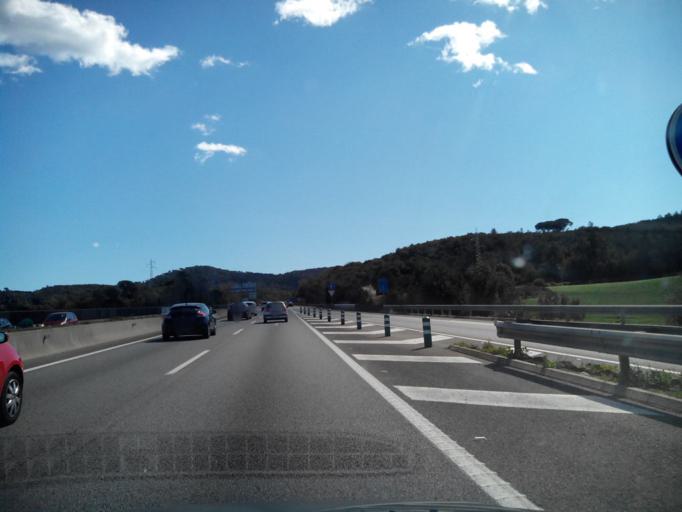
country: ES
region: Catalonia
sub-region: Provincia de Barcelona
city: La Roca del Valles
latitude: 41.5919
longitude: 2.3435
